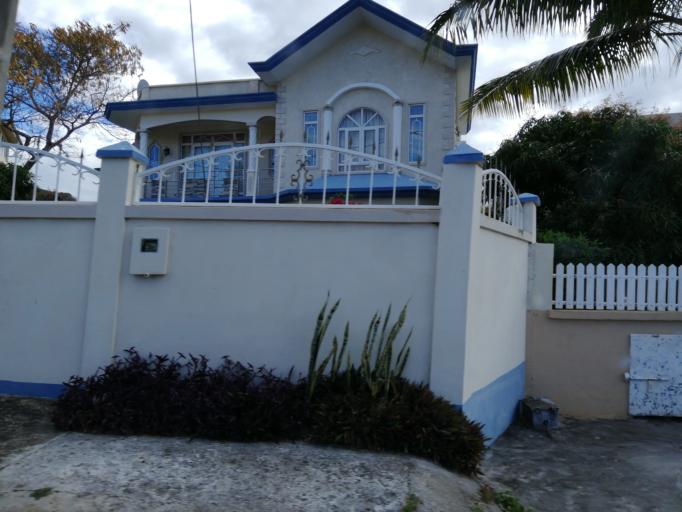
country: MU
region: Moka
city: Pailles
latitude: -20.2026
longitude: 57.4677
